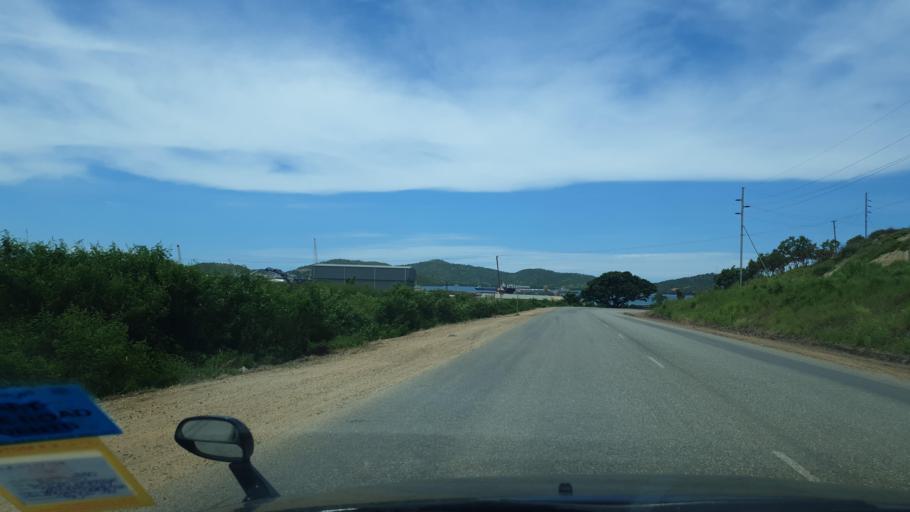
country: PG
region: National Capital
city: Port Moresby
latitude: -9.4179
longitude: 147.0996
